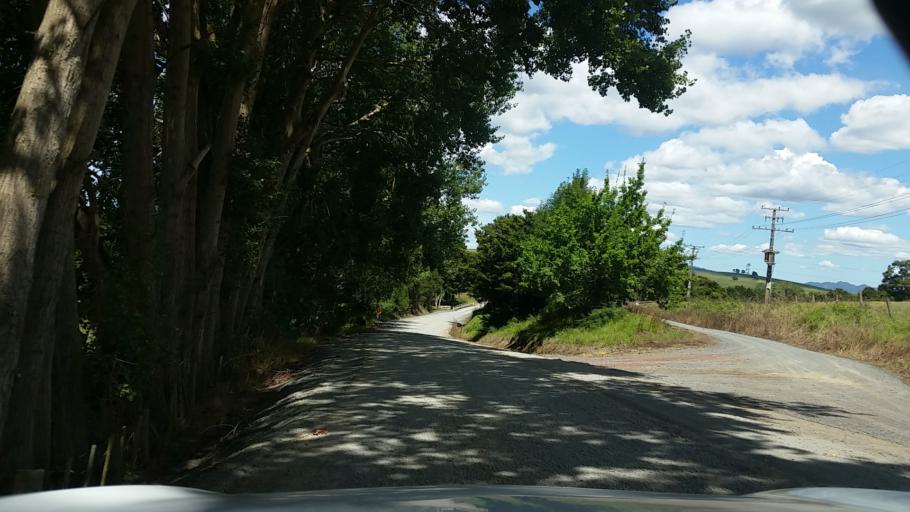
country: NZ
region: Northland
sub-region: Whangarei
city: Maungatapere
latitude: -35.6961
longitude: 174.1445
